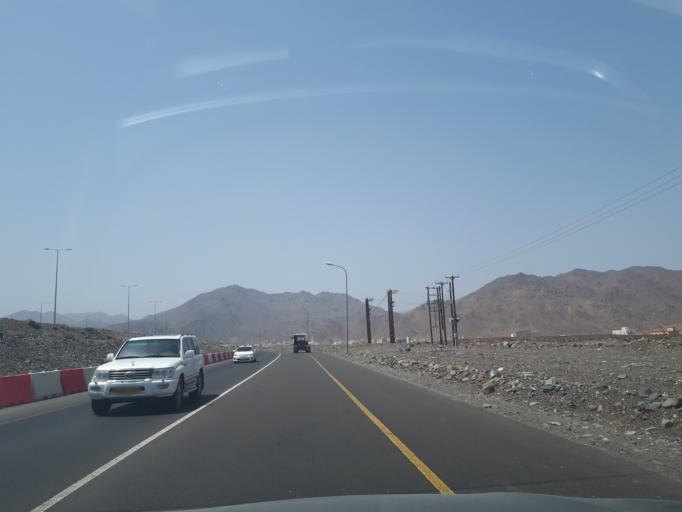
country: OM
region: Muhafazat ad Dakhiliyah
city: Sufalat Sama'il
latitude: 23.2727
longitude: 58.1050
